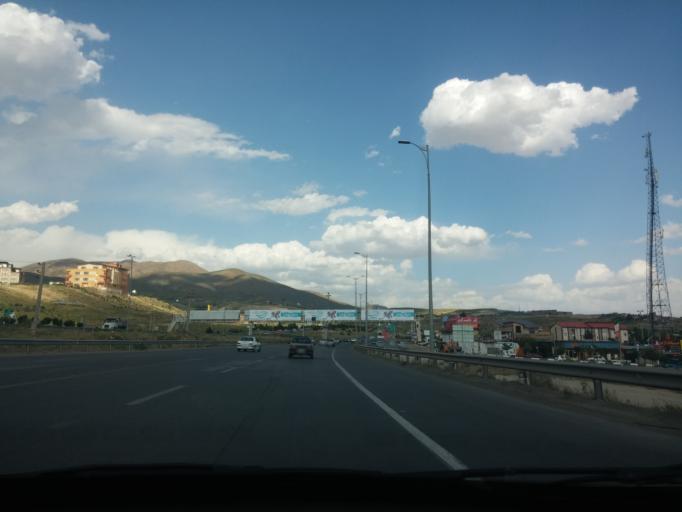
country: IR
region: Tehran
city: Damavand
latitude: 35.7194
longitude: 51.9167
